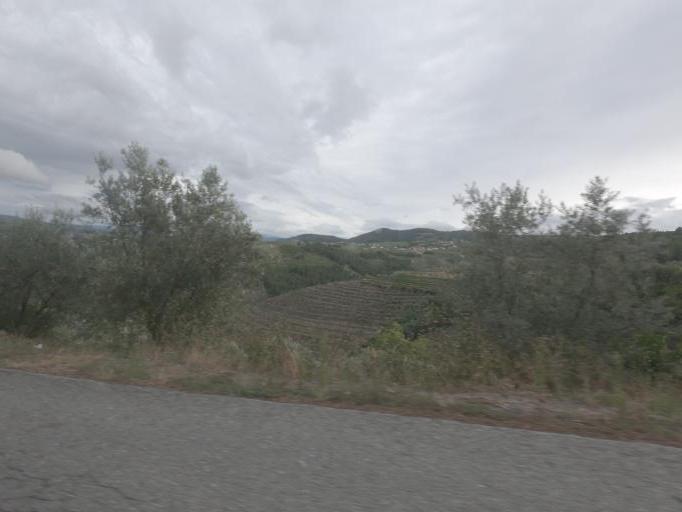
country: PT
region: Vila Real
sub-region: Sabrosa
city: Sabrosa
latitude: 41.2634
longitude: -7.5650
